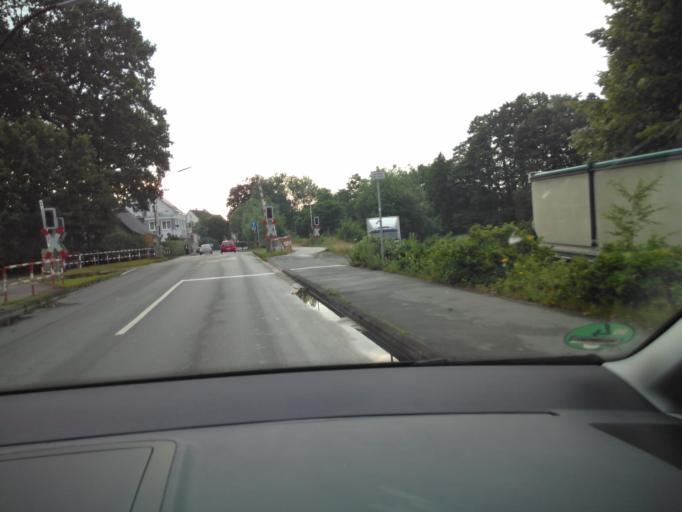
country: DE
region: North Rhine-Westphalia
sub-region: Regierungsbezirk Detmold
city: Oerlinghausen
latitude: 51.9032
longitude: 8.6163
